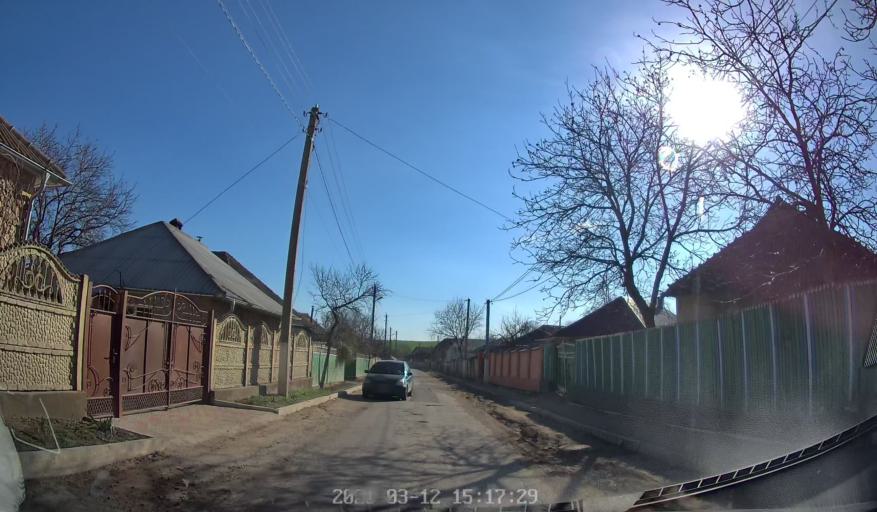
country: MD
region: Chisinau
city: Ciorescu
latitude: 47.2205
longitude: 28.9351
